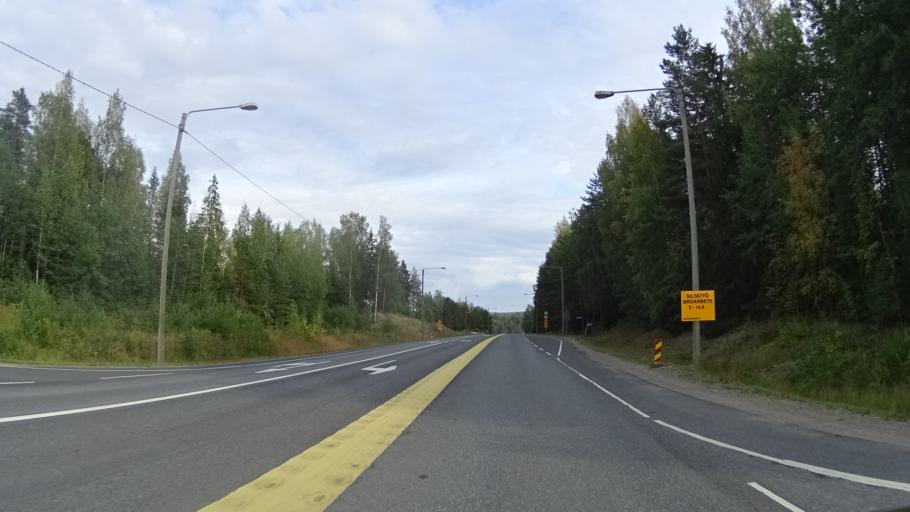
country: FI
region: Haeme
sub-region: Haemeenlinna
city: Parola
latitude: 61.0437
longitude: 24.2428
